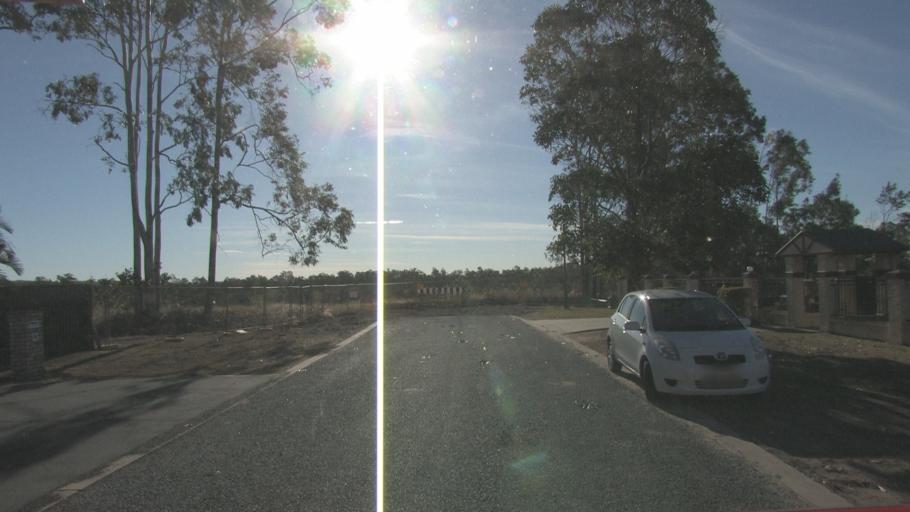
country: AU
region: Queensland
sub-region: Logan
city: North Maclean
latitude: -27.7321
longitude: 152.9705
